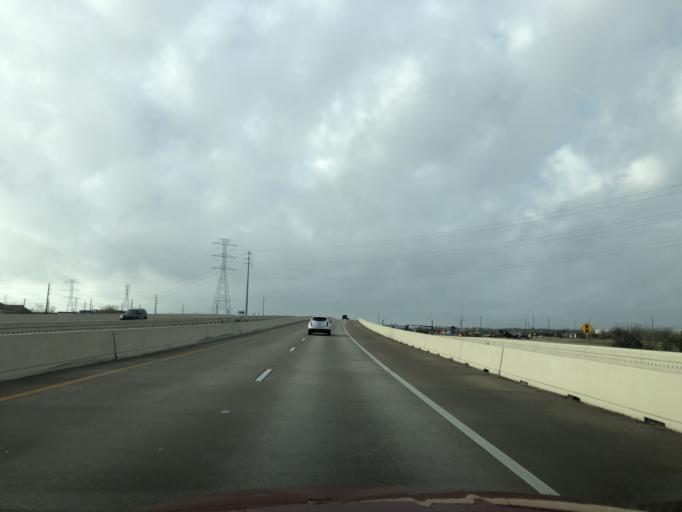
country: US
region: Texas
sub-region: Harris County
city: Katy
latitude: 29.8344
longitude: -95.7588
